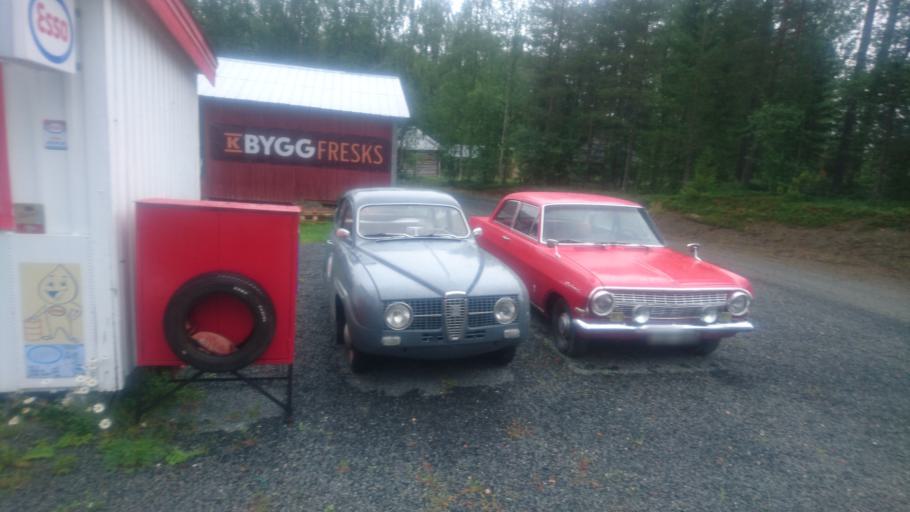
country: SE
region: Vaesterbotten
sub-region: Storumans Kommun
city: Fristad
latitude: 65.4310
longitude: 16.2428
